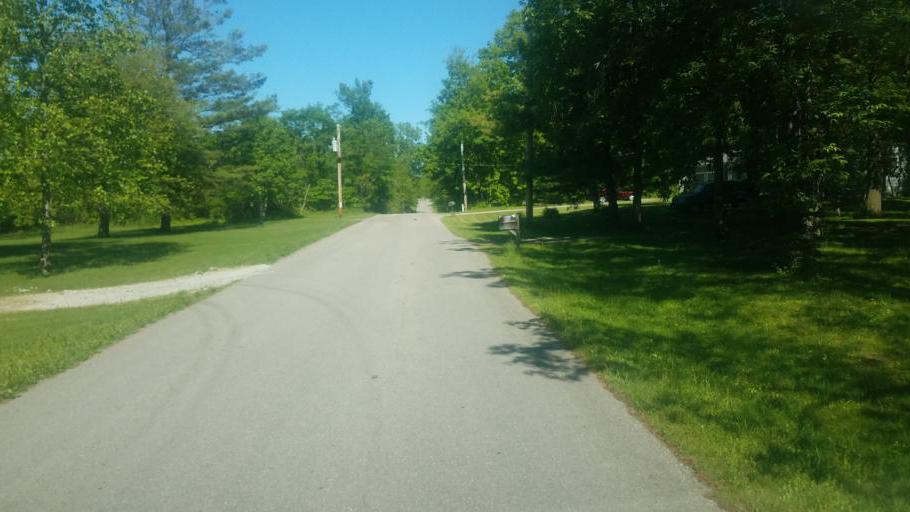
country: US
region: Ohio
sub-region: Logan County
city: Northwood
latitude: 40.4363
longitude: -83.7332
